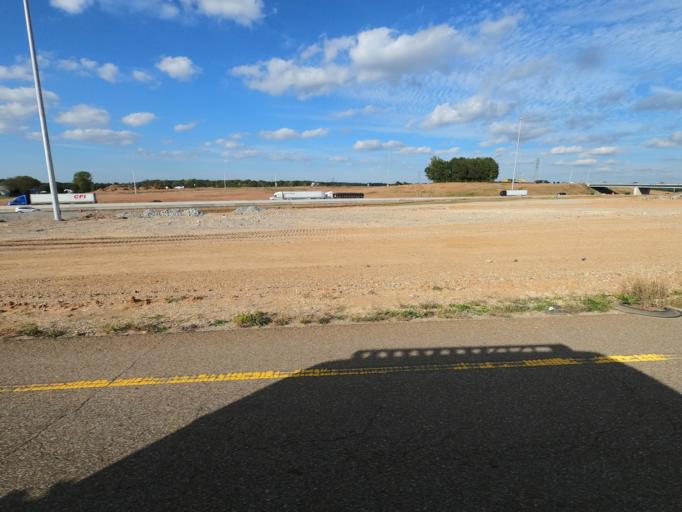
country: US
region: Tennessee
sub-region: Madison County
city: Jackson
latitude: 35.6776
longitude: -88.7830
